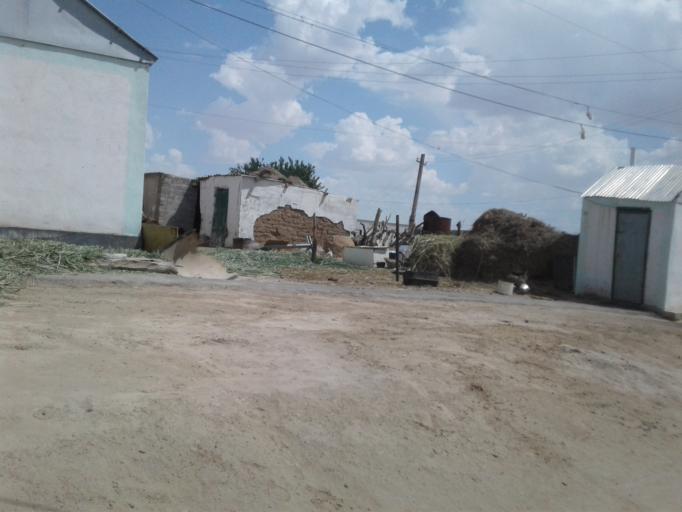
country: TM
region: Ahal
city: Abadan
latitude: 38.7656
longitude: 58.4936
